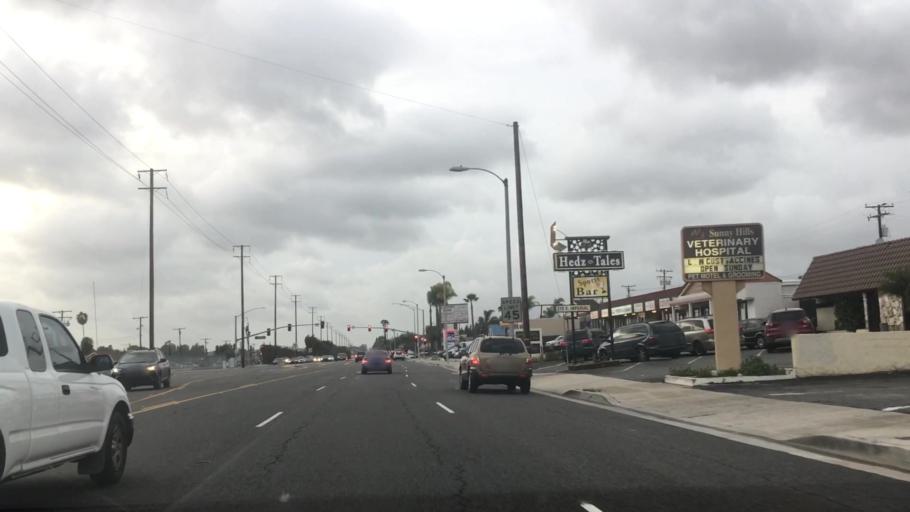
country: US
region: California
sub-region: Orange County
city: La Habra
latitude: 33.9174
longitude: -117.9440
